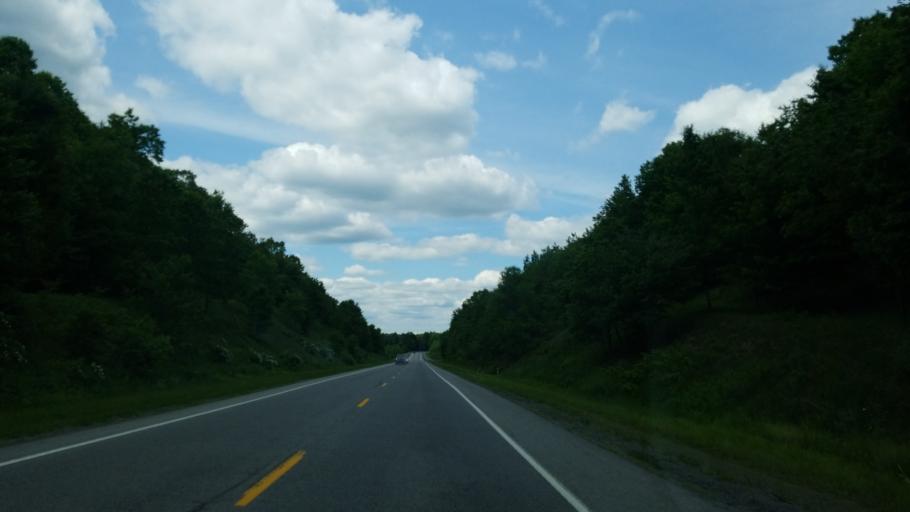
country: US
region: Pennsylvania
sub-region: Clearfield County
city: Hyde
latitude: 40.9277
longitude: -78.3829
